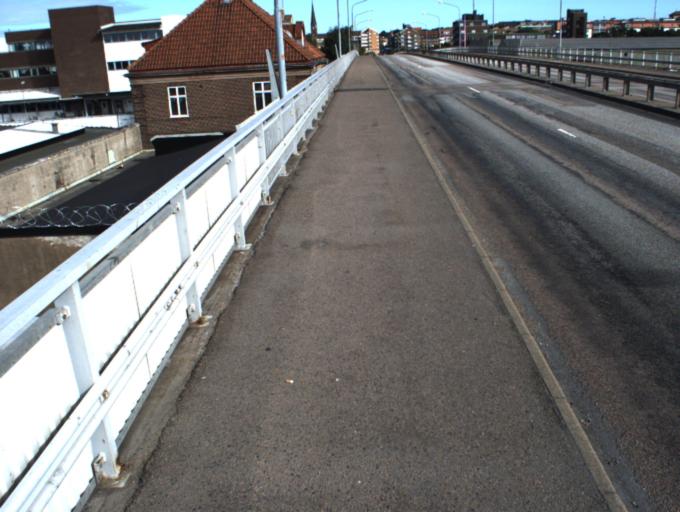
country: SE
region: Skane
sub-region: Helsingborg
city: Helsingborg
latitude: 56.0321
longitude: 12.7082
